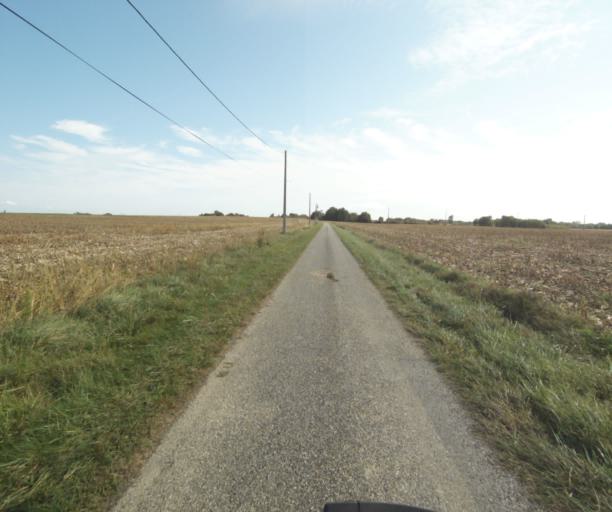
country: FR
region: Midi-Pyrenees
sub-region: Departement du Tarn-et-Garonne
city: Verdun-sur-Garonne
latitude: 43.8465
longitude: 1.1842
